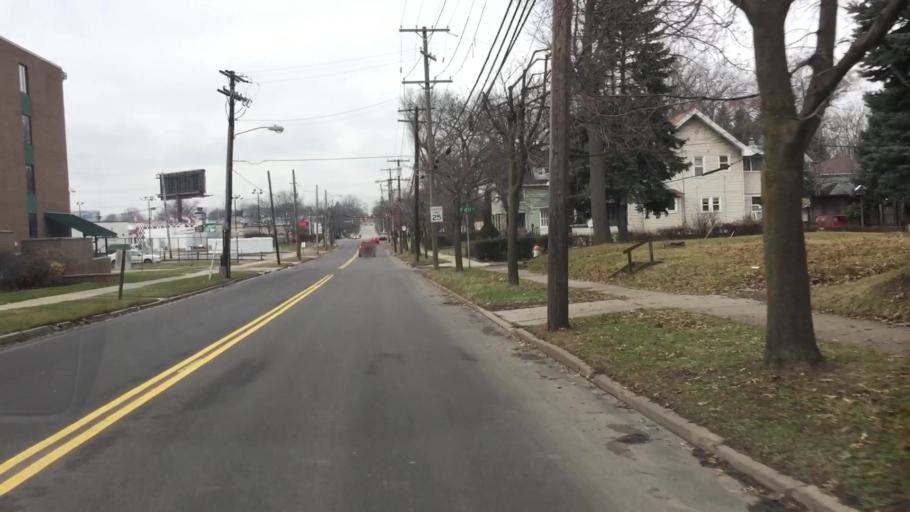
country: US
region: Ohio
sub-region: Summit County
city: Akron
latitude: 41.0767
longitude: -81.4931
